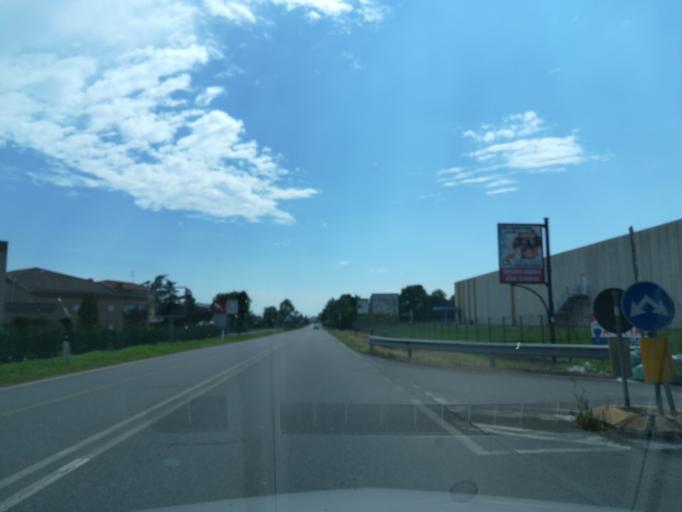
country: IT
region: Lombardy
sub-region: Provincia di Bergamo
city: Almenno San Bartolomeo
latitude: 45.7350
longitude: 9.5796
